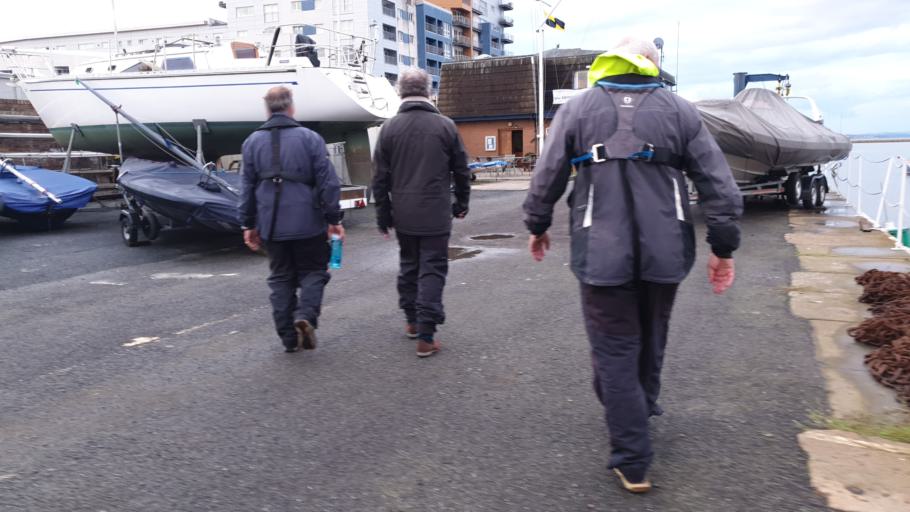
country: GB
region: Scotland
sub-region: Edinburgh
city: Edinburgh
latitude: 55.9827
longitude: -3.2231
